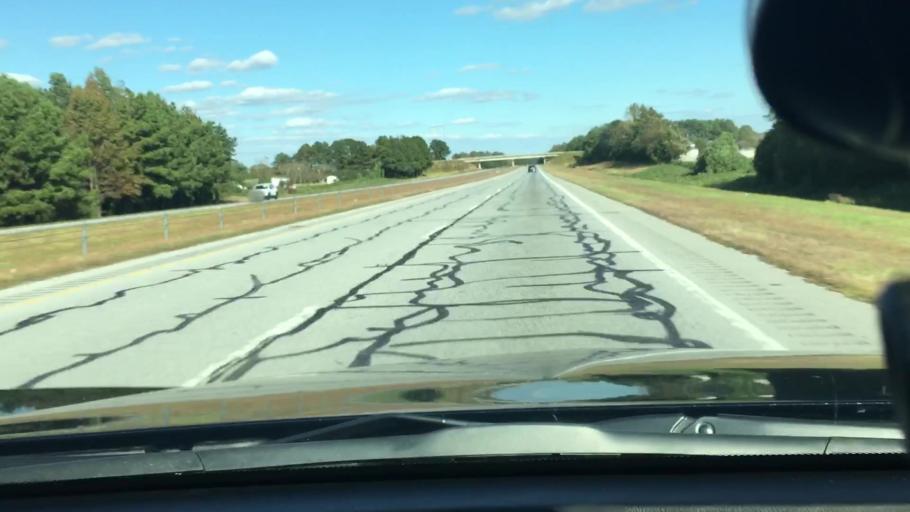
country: US
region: North Carolina
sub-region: Pitt County
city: Farmville
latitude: 35.6016
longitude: -77.5306
